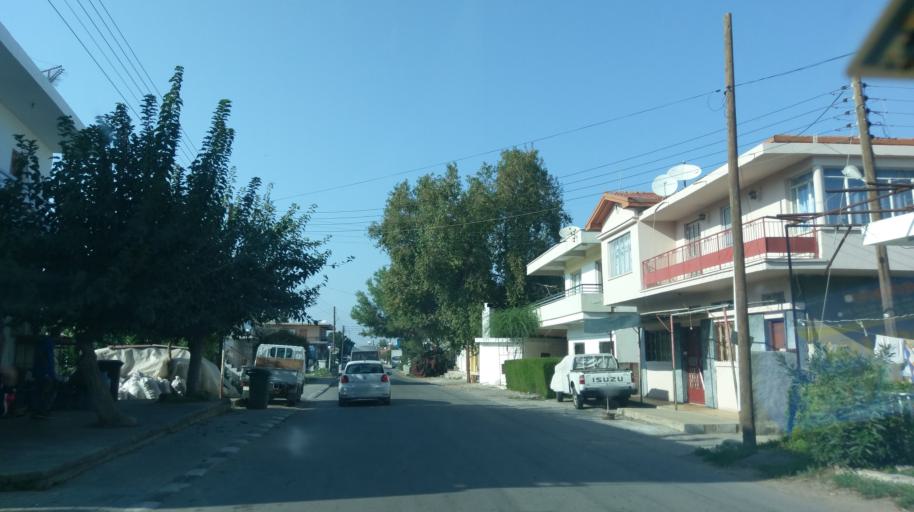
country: CY
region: Lefkosia
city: Lefka
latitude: 35.1432
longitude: 32.8084
